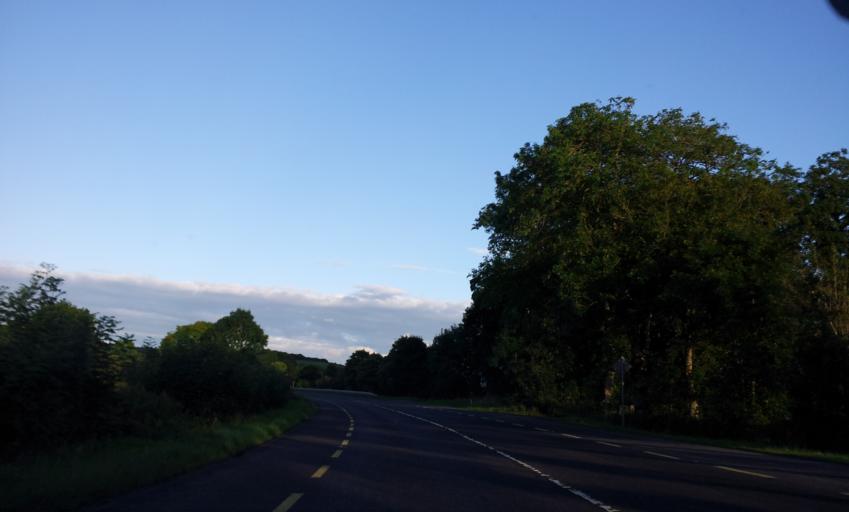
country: IE
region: Munster
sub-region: County Limerick
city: Abbeyfeale
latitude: 52.3834
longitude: -9.2263
